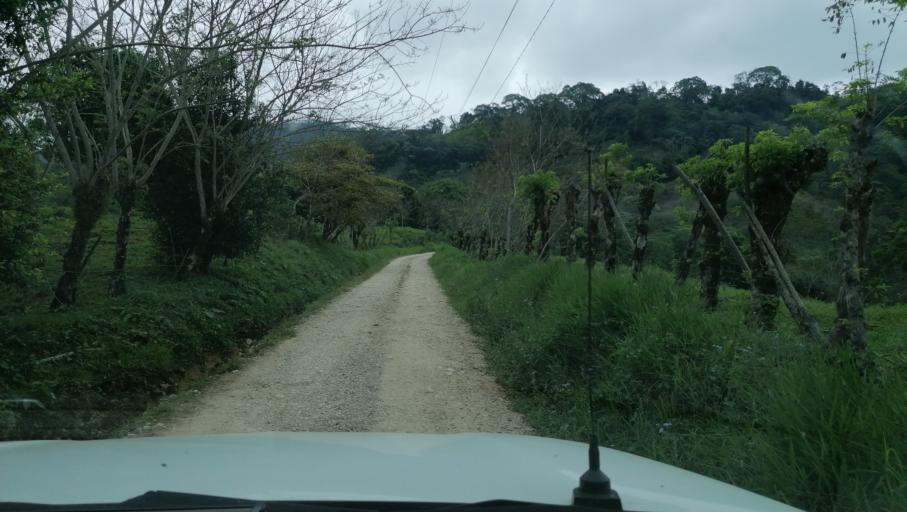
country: MX
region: Chiapas
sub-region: Ocotepec
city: San Pablo Huacano
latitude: 17.2737
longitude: -93.2407
